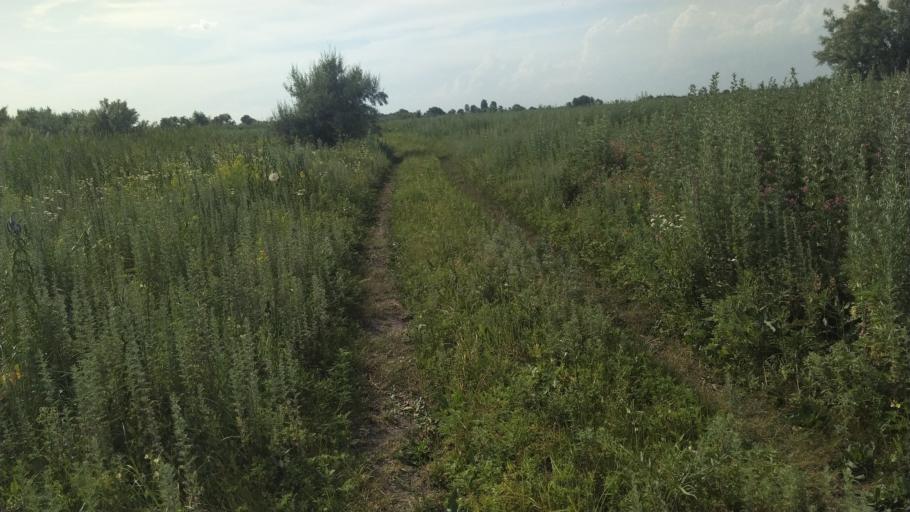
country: RU
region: Rostov
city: Kuleshovka
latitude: 47.1259
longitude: 39.6196
